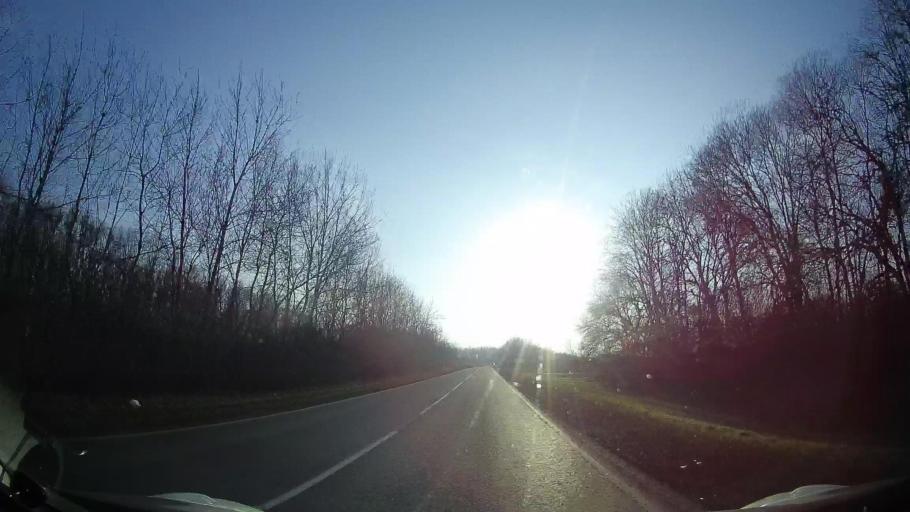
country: RU
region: Rostov
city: Ol'ginskaya
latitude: 47.1650
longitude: 39.9373
